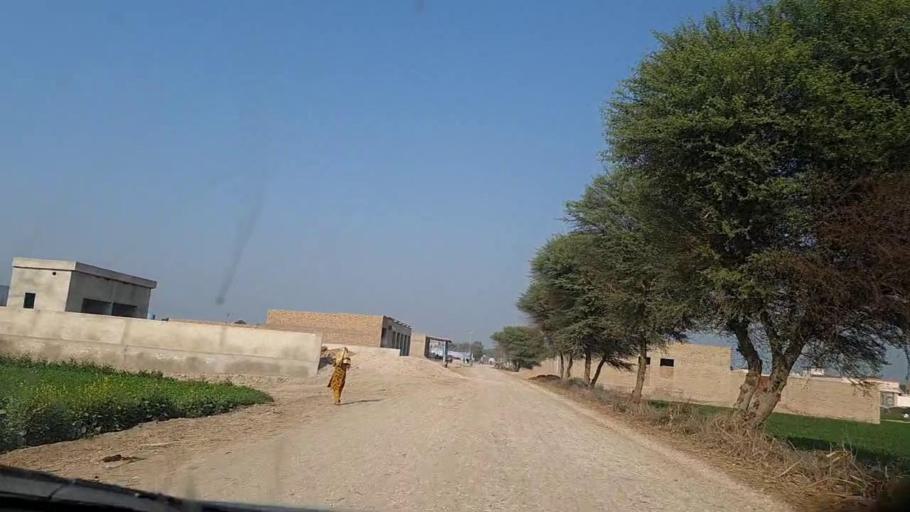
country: PK
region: Sindh
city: Moro
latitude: 26.7868
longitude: 67.9386
